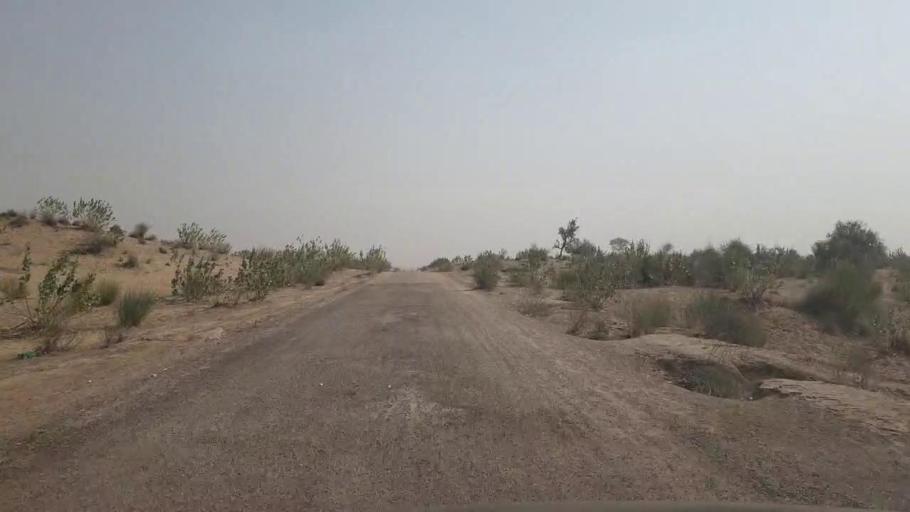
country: PK
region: Sindh
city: Chor
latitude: 25.5970
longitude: 70.0019
